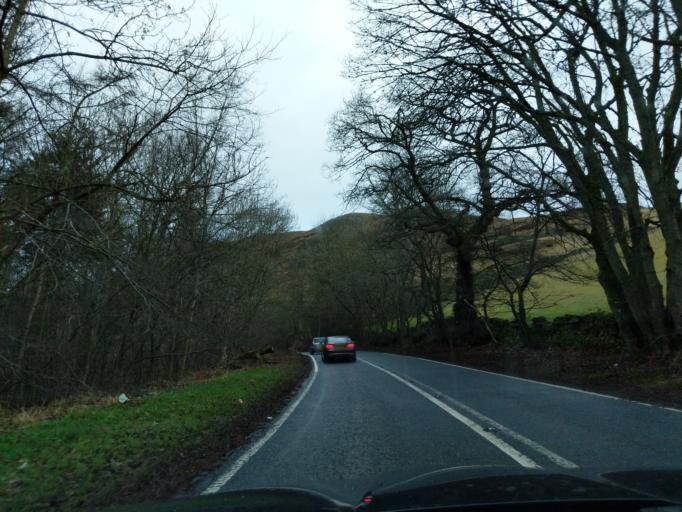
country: GB
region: Scotland
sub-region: The Scottish Borders
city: Galashiels
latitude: 55.6610
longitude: -2.8603
